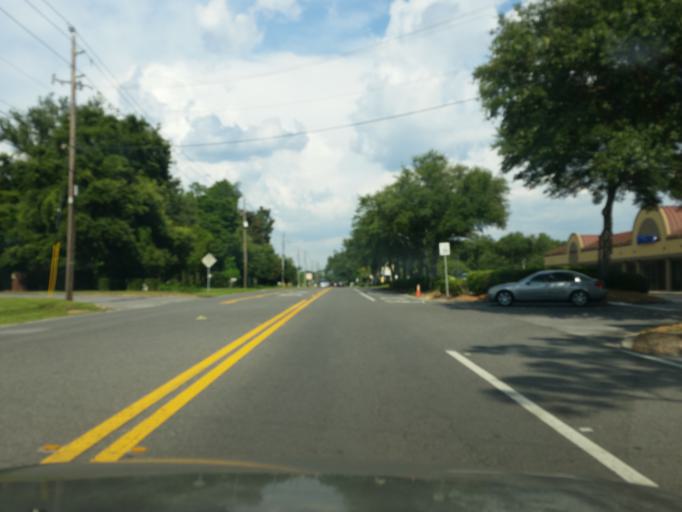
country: US
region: Florida
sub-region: Escambia County
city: Ferry Pass
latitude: 30.4941
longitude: -87.2275
